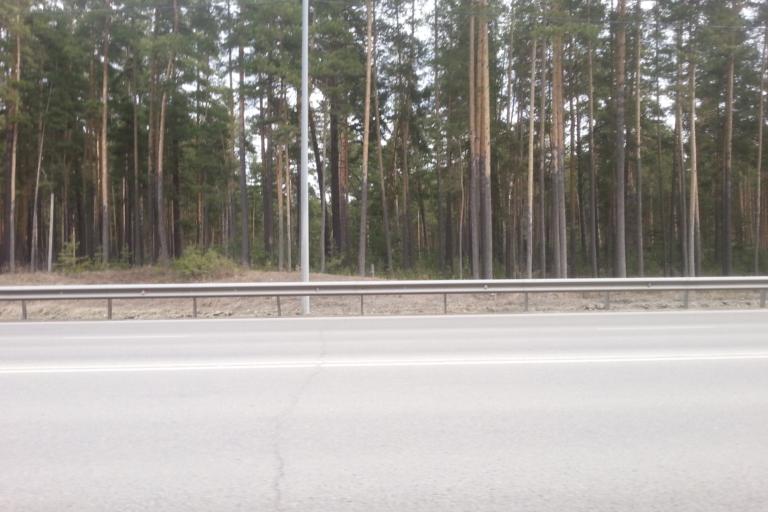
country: RU
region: Altai Krai
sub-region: Gorod Barnaulskiy
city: Barnaul
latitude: 53.3241
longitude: 83.7051
